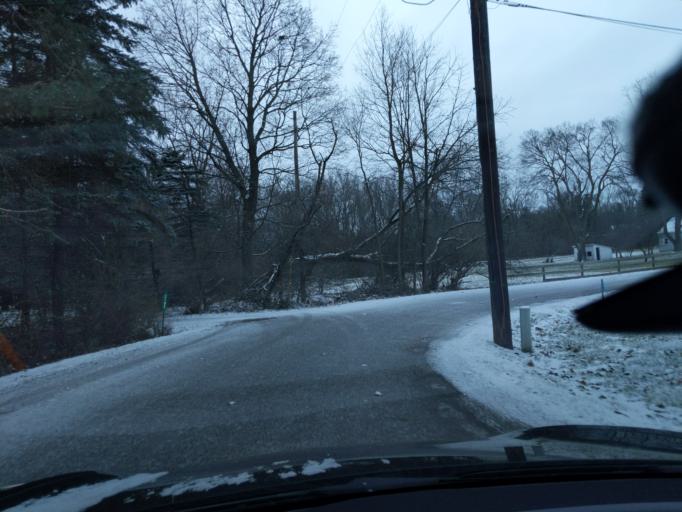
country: US
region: Michigan
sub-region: Ingham County
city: Okemos
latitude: 42.7166
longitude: -84.4318
